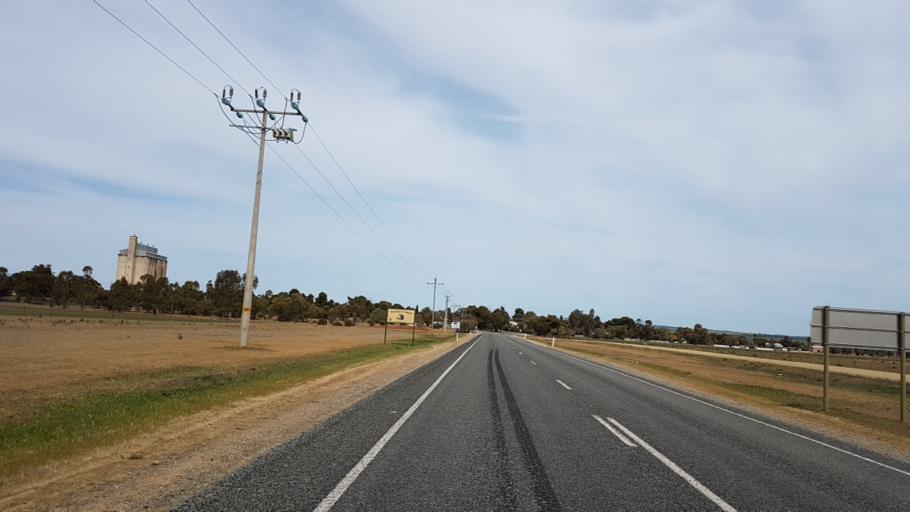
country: AU
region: South Australia
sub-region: Peterborough
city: Peterborough
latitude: -33.0234
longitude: 138.7503
